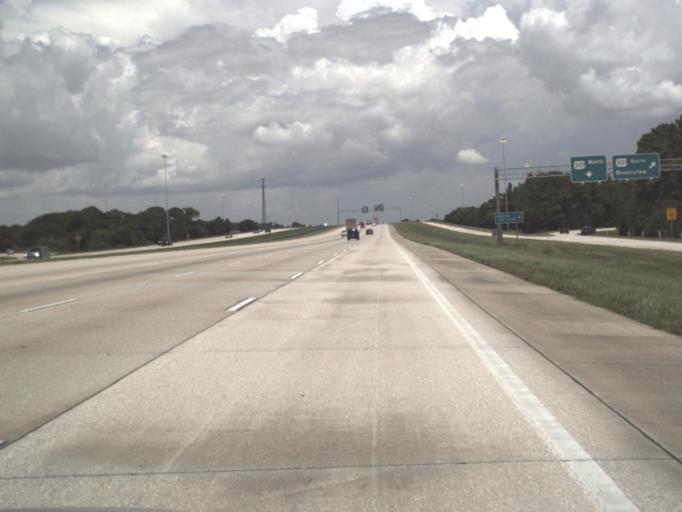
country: US
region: Florida
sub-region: Hillsborough County
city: Progress Village
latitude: 27.8971
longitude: -82.3468
